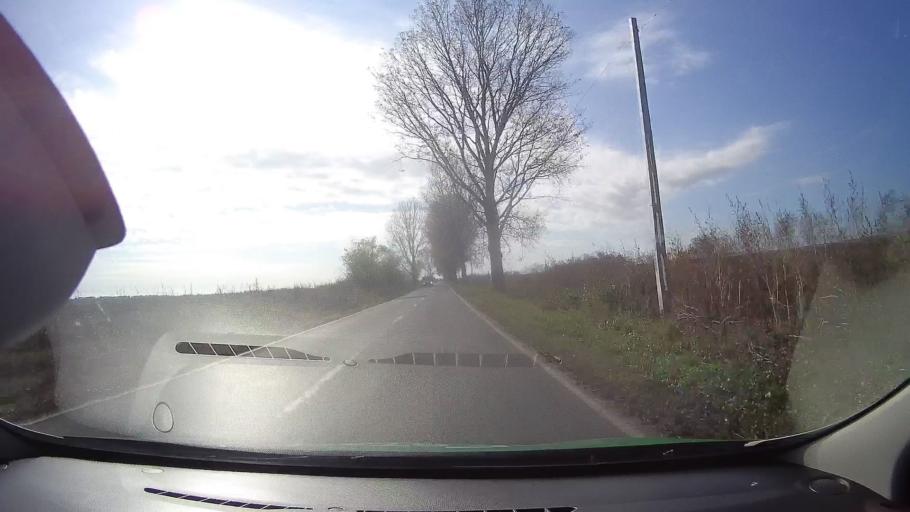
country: RO
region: Tulcea
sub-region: Comuna Valea Nucarilor
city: Agighiol
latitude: 44.9899
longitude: 28.8853
